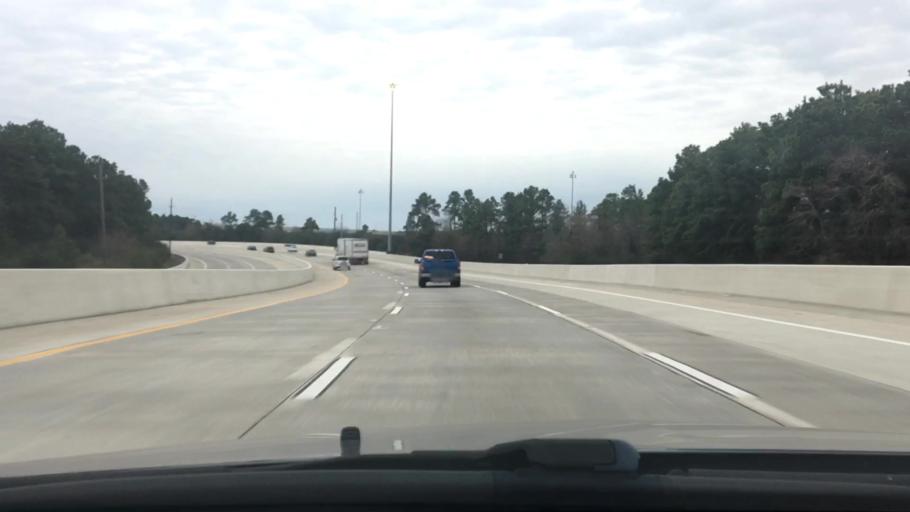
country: US
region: Texas
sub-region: Harris County
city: Spring
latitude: 30.0730
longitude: -95.4119
